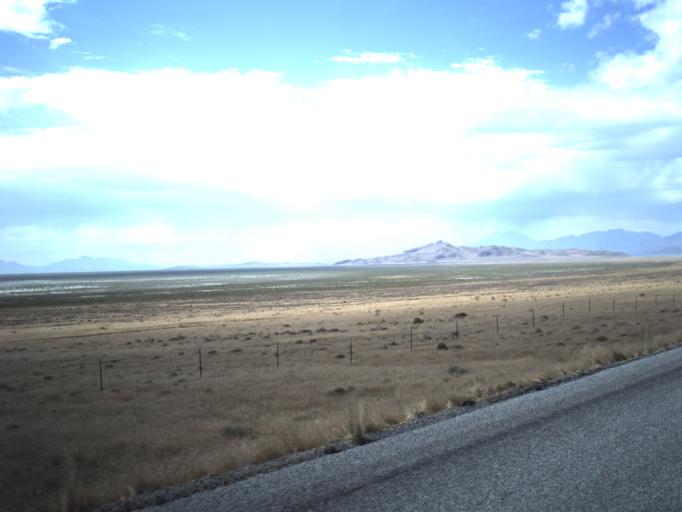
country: US
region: Utah
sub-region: Tooele County
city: Wendover
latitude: 41.4508
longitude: -113.6706
